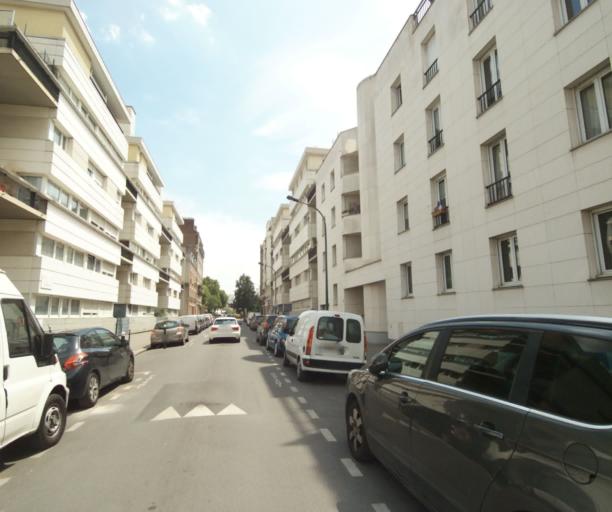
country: FR
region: Ile-de-France
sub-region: Departement des Hauts-de-Seine
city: Asnieres-sur-Seine
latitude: 48.9145
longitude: 2.2867
